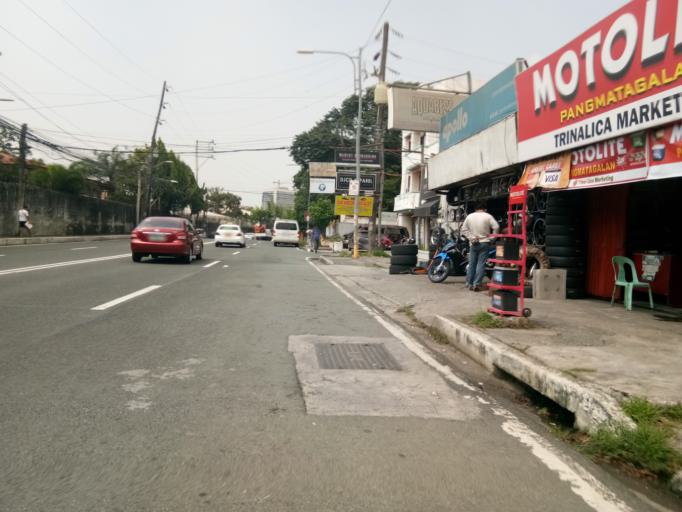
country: PH
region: Metro Manila
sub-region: San Juan
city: San Juan
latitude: 14.6089
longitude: 121.0450
